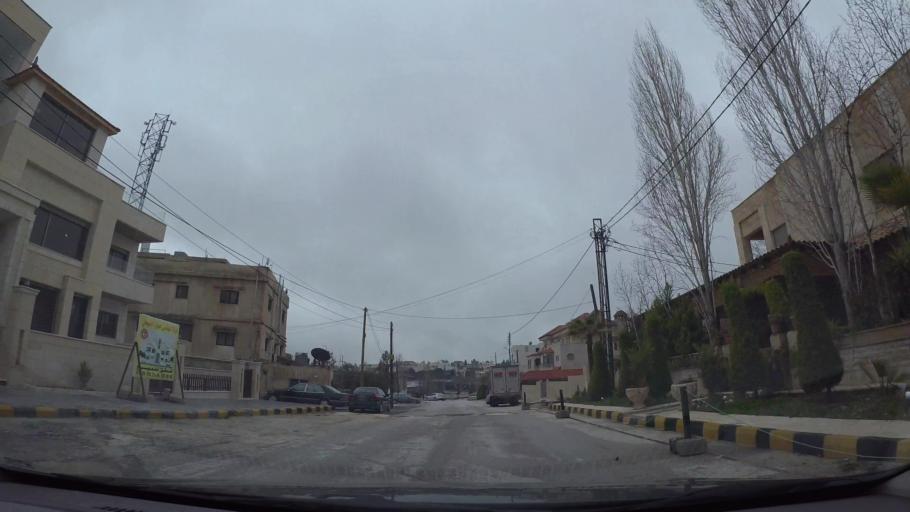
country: JO
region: Amman
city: Al Bunayyat ash Shamaliyah
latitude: 31.9429
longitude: 35.8845
